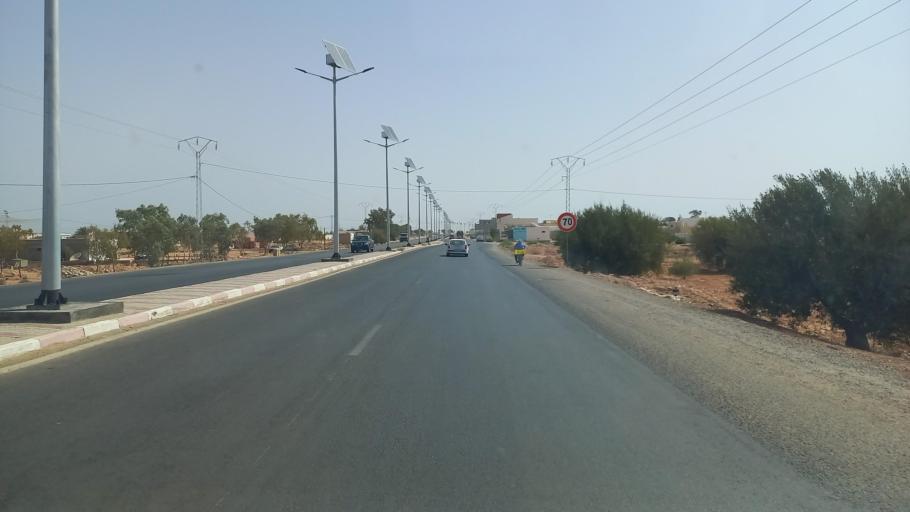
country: TN
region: Madanin
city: Medenine
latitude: 33.3579
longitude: 10.5490
